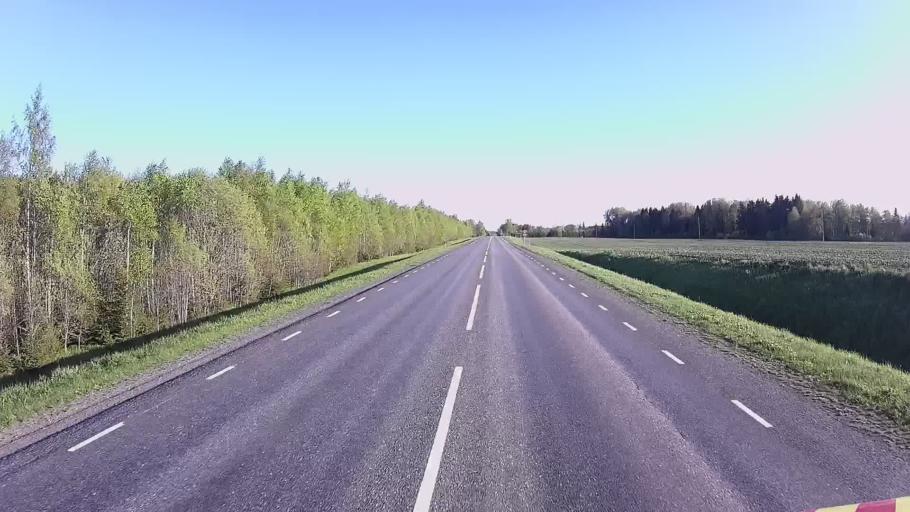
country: EE
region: Viljandimaa
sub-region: Viljandi linn
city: Viljandi
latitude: 58.4179
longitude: 25.5968
